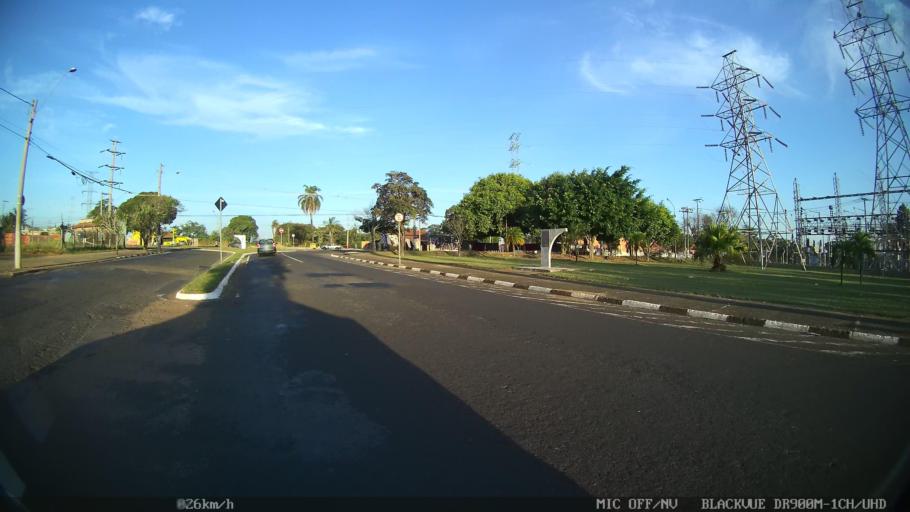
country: BR
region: Sao Paulo
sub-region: Franca
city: Franca
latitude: -20.5151
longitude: -47.3799
